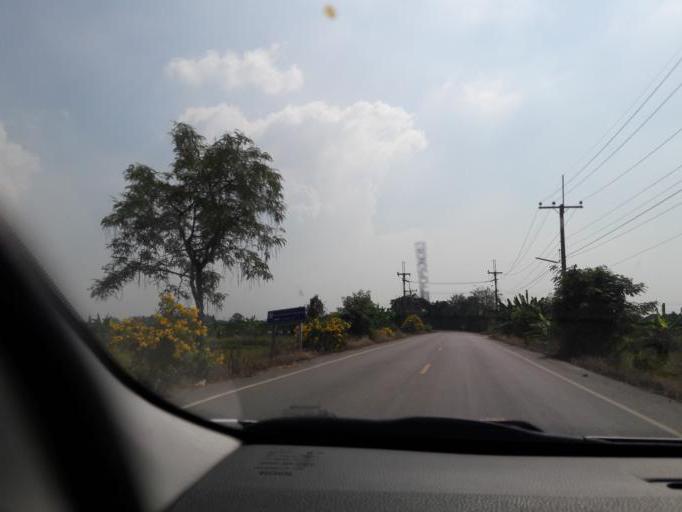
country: TH
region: Ang Thong
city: Ang Thong
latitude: 14.5808
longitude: 100.4282
